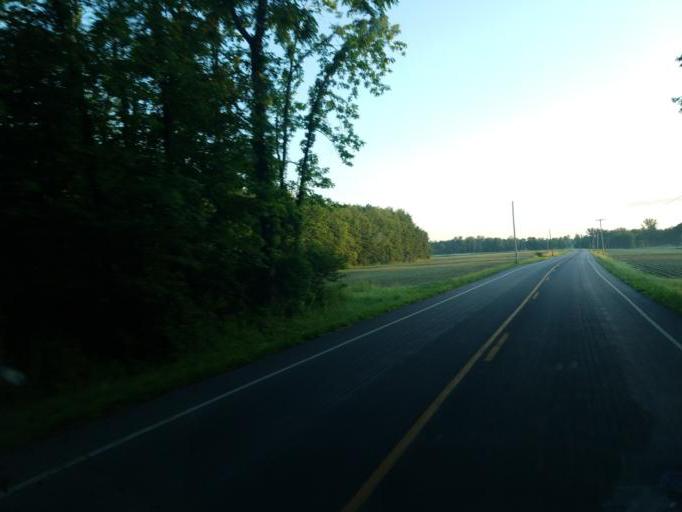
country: US
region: New York
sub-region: Wayne County
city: Clyde
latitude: 43.0685
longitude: -76.8910
